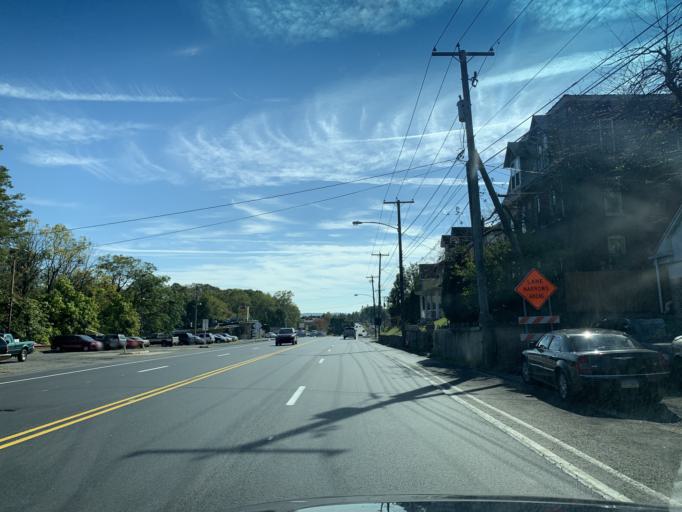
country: US
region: Pennsylvania
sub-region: Berks County
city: Saint Lawrence
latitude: 40.3245
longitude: -75.8768
